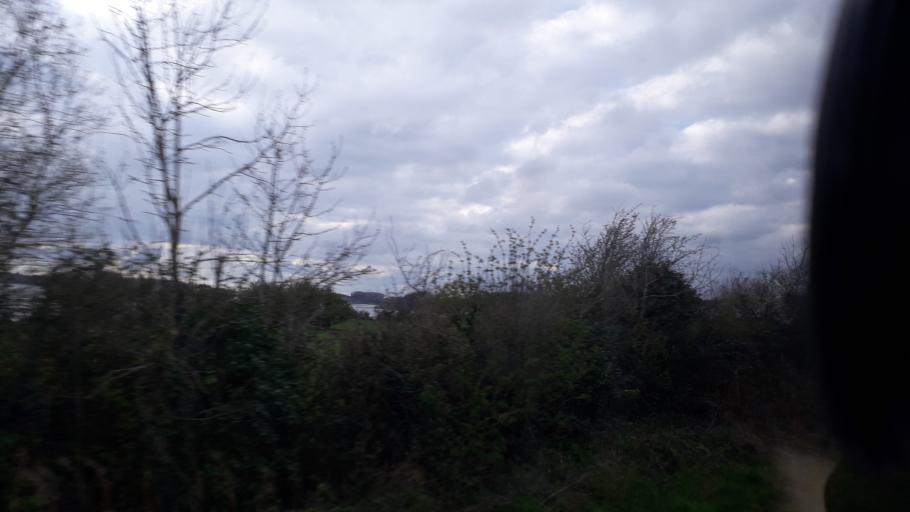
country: IE
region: Leinster
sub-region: An Iarmhi
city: An Muileann gCearr
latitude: 53.5846
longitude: -7.3809
